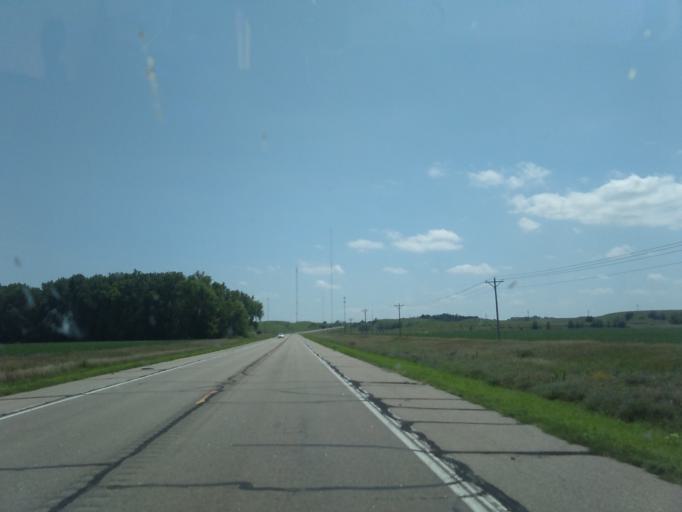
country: US
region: Nebraska
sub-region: Dawson County
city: Lexington
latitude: 40.7132
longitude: -99.7874
